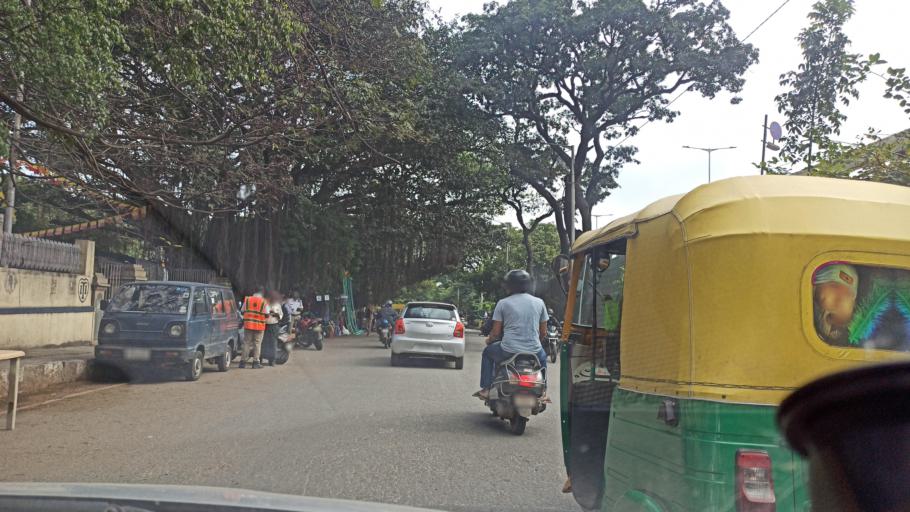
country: IN
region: Karnataka
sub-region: Bangalore Urban
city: Bangalore
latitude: 13.0033
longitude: 77.6815
